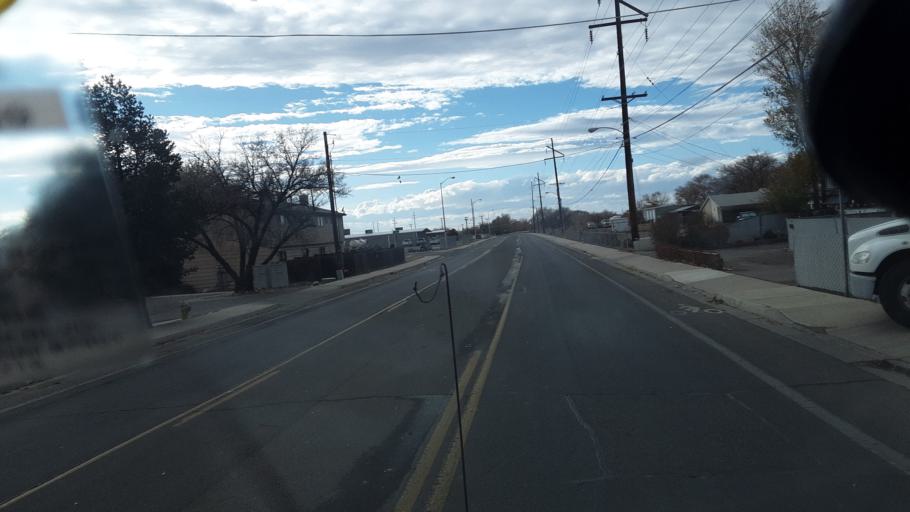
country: US
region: New Mexico
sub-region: San Juan County
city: Farmington
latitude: 36.7267
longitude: -108.1849
